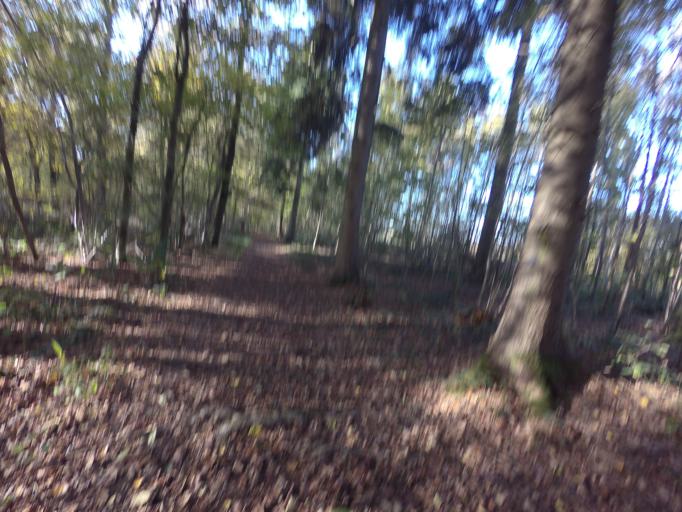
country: NL
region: Limburg
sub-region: Gemeente Simpelveld
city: Simpelveld
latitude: 50.8046
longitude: 5.9737
